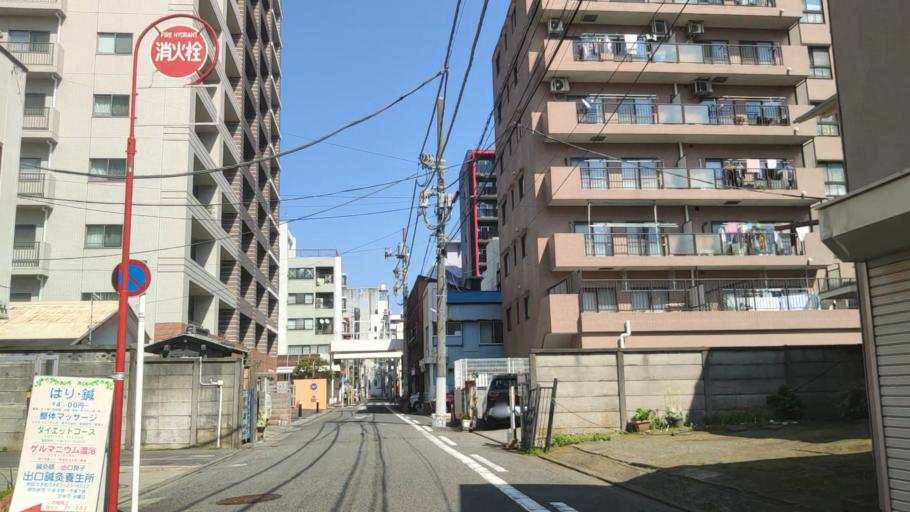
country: JP
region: Kanagawa
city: Hiratsuka
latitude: 35.3307
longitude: 139.3463
